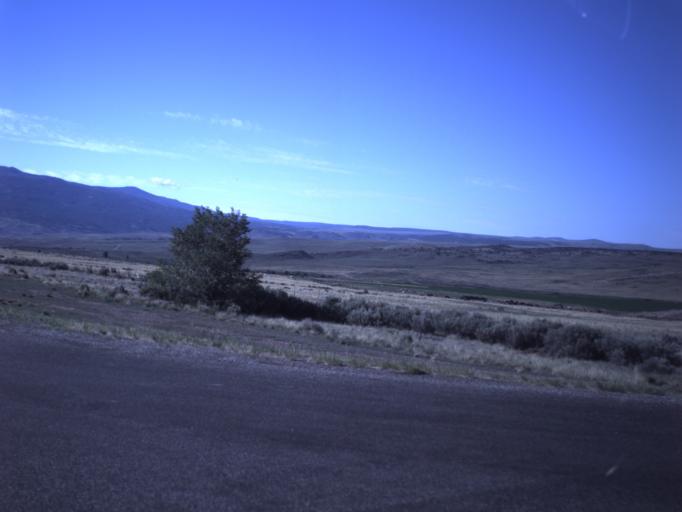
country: US
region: Utah
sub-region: Wayne County
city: Loa
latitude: 38.3535
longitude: -111.5739
